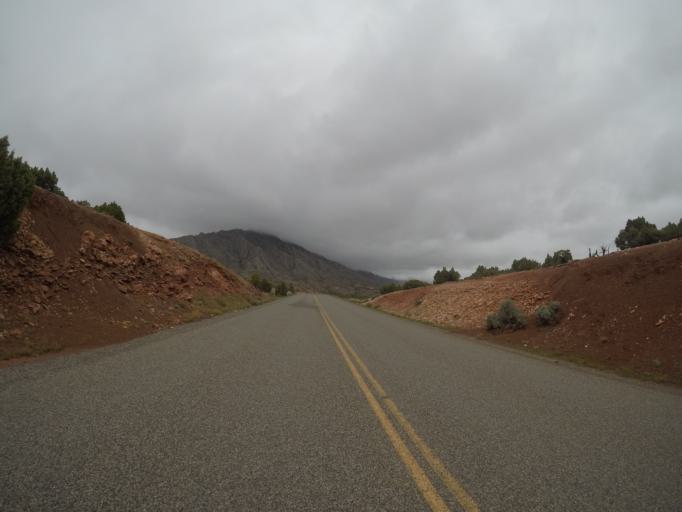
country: US
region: Wyoming
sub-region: Big Horn County
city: Lovell
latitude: 45.0234
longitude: -108.2546
